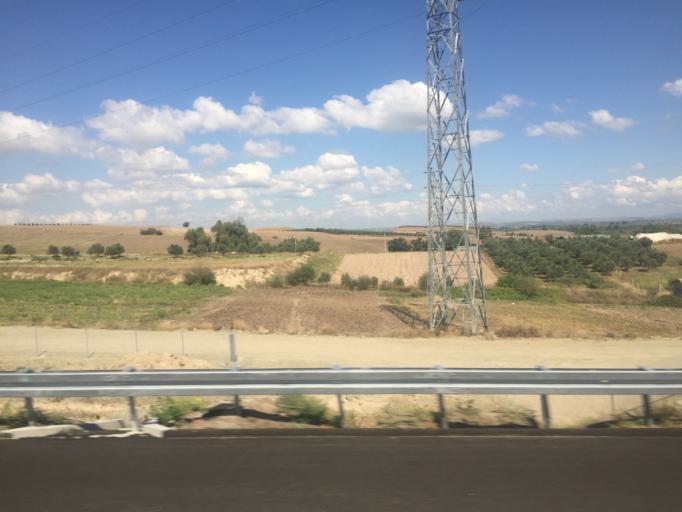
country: TR
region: Balikesir
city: Gobel
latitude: 40.0481
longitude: 28.2280
